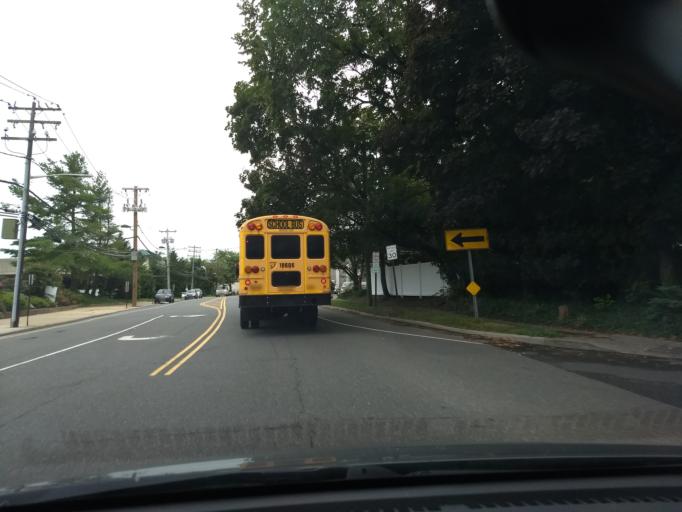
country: US
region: New York
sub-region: Nassau County
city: Great Neck Gardens
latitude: 40.8003
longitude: -73.7148
